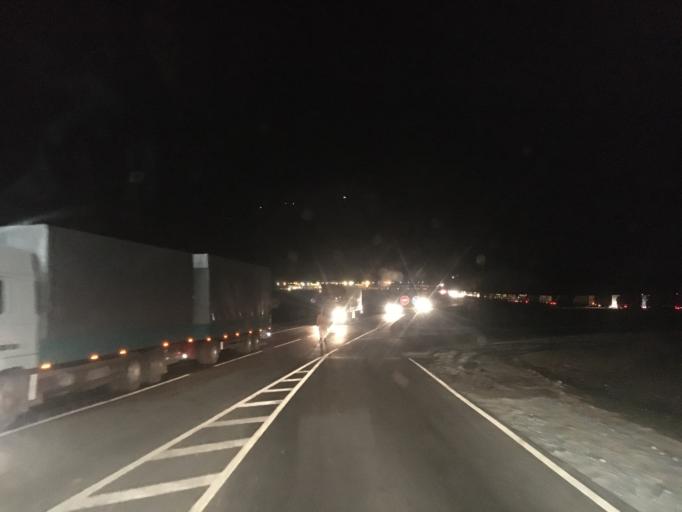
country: KZ
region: Batys Qazaqstan
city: Peremetnoe
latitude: 51.6672
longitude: 51.0053
